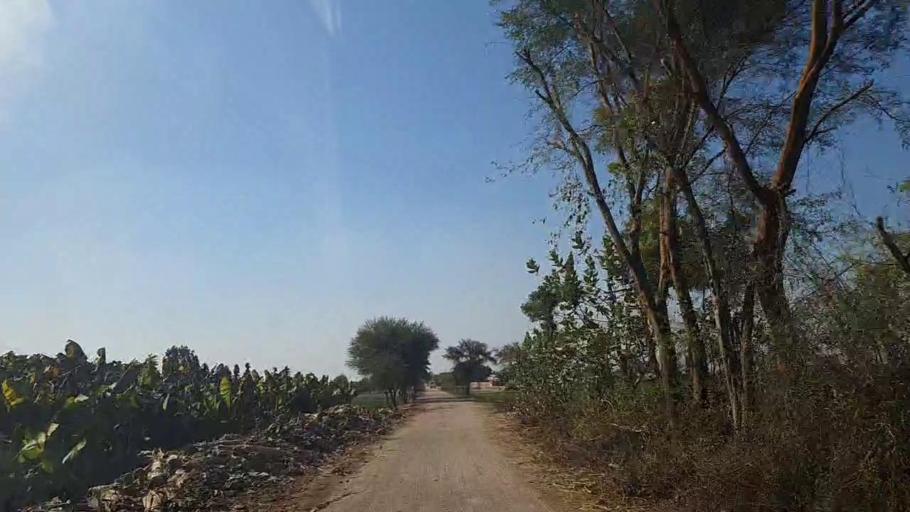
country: PK
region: Sindh
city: Sakrand
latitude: 26.2628
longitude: 68.2187
